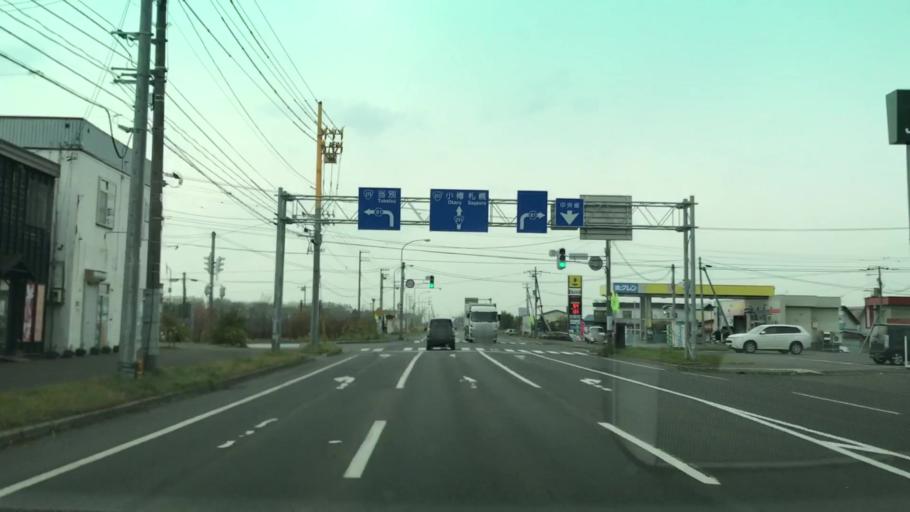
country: JP
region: Hokkaido
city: Ishikari
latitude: 43.2441
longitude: 141.3711
